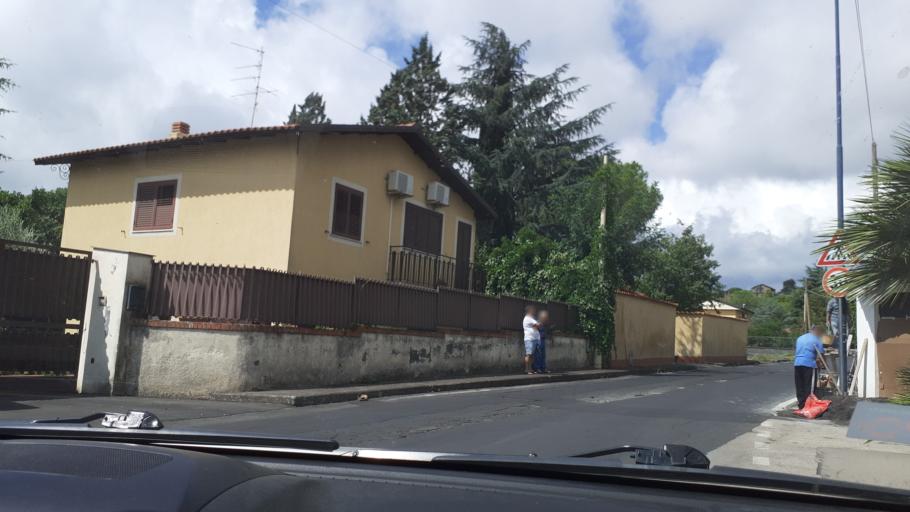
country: IT
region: Sicily
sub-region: Catania
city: Pedara
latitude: 37.6080
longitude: 15.0611
